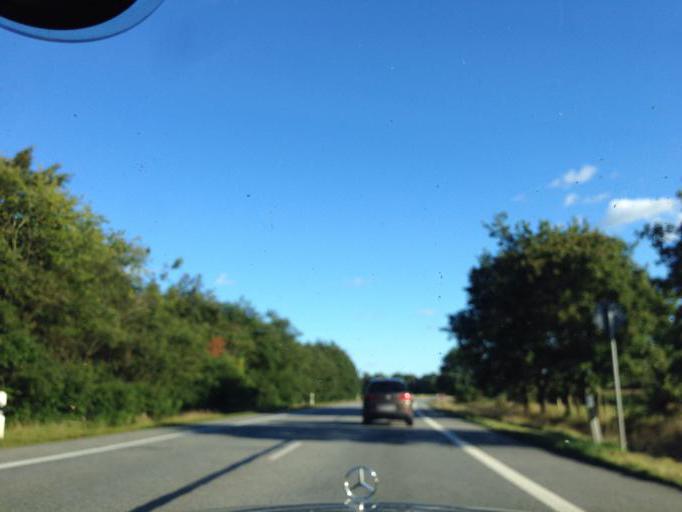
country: DE
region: Schleswig-Holstein
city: Rickling
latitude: 54.0133
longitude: 10.1696
